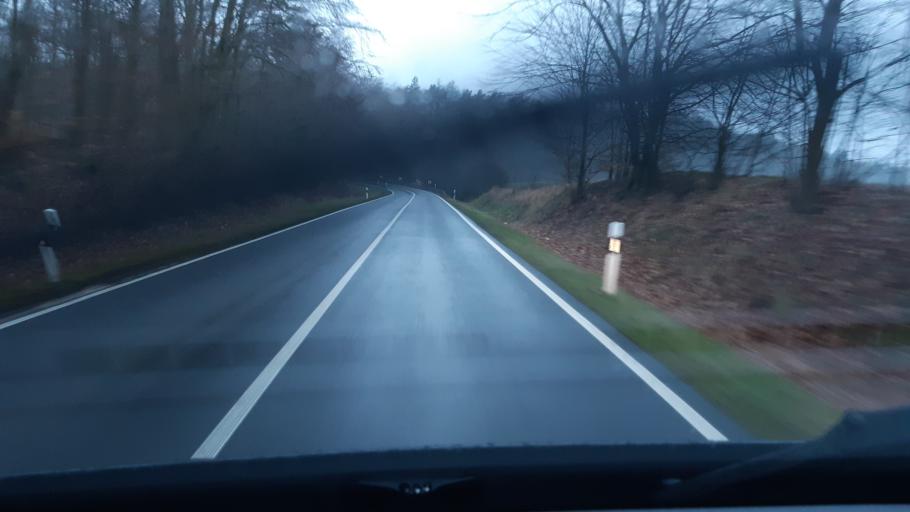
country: DE
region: Brandenburg
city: Milmersdorf
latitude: 53.1494
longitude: 13.5800
